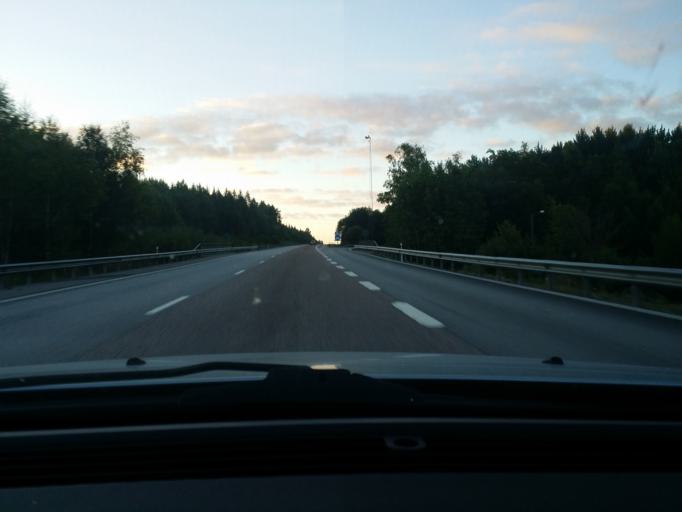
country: SE
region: Uppsala
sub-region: Enkopings Kommun
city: Dalby
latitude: 59.6204
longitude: 17.3907
